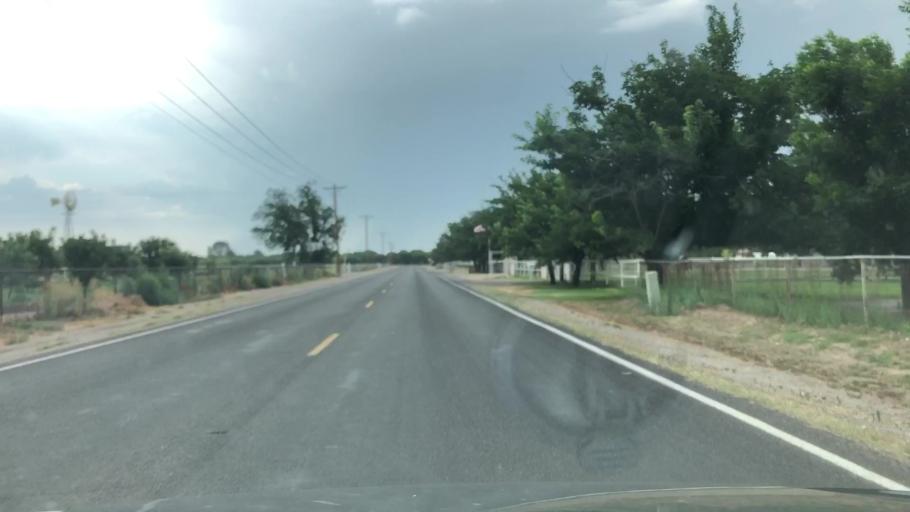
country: US
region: Texas
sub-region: El Paso County
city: Canutillo
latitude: 31.9281
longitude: -106.6287
